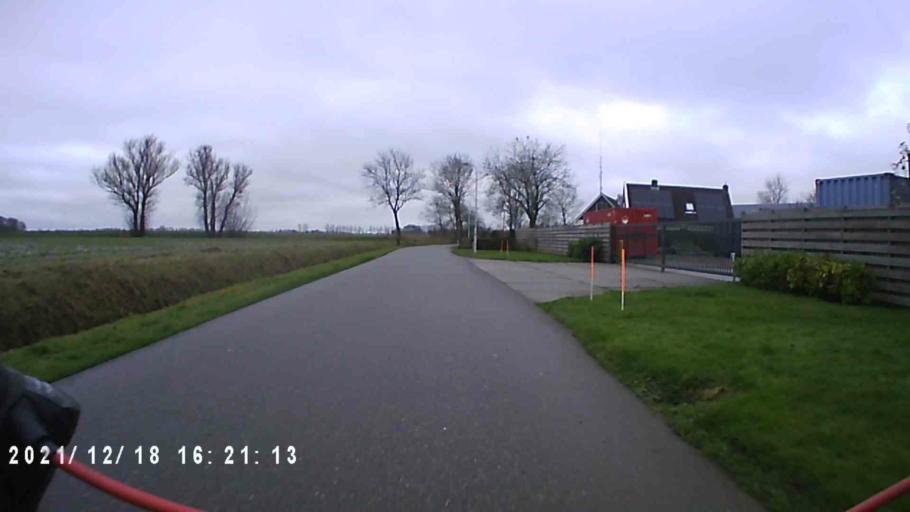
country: NL
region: Friesland
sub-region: Gemeente Dongeradeel
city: Dokkum
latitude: 53.3791
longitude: 6.0475
